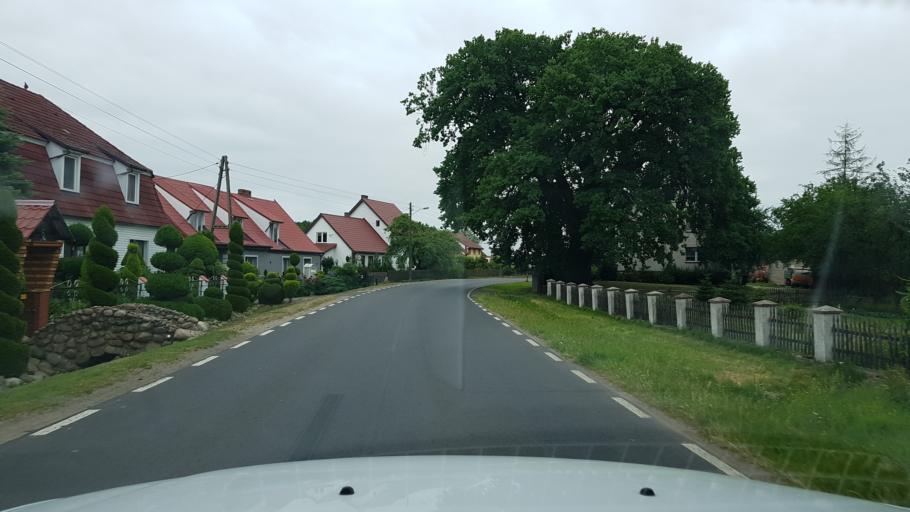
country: PL
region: West Pomeranian Voivodeship
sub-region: Powiat gryficki
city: Brojce
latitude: 53.9391
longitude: 15.4056
